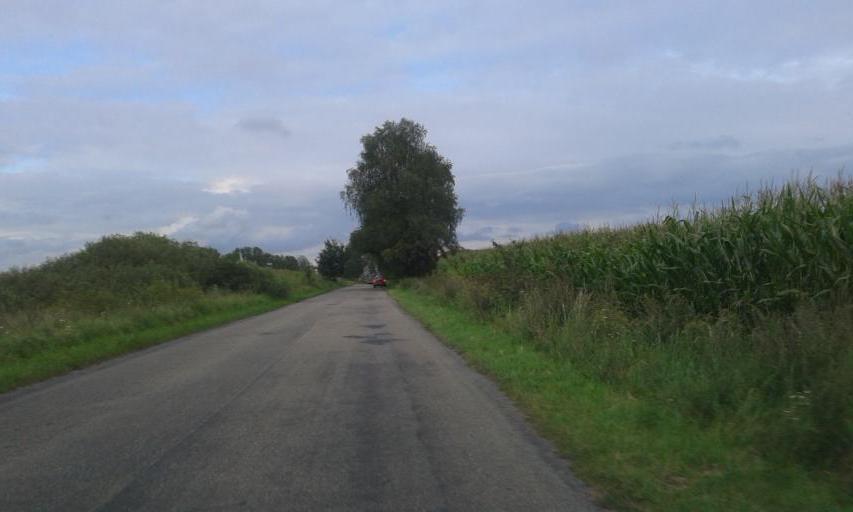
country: PL
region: West Pomeranian Voivodeship
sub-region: Powiat szczecinecki
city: Lubowo
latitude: 53.5851
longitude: 16.4153
